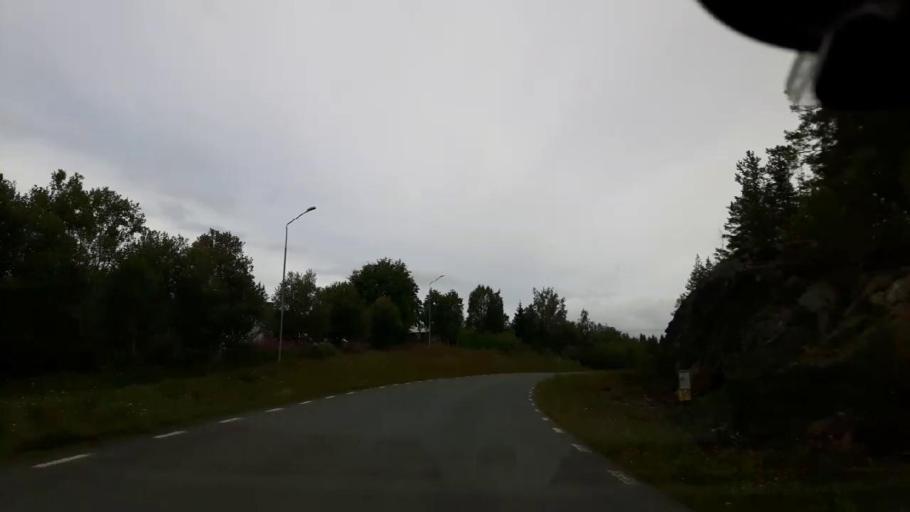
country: SE
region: Jaemtland
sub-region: Krokoms Kommun
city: Valla
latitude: 63.6534
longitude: 13.8284
